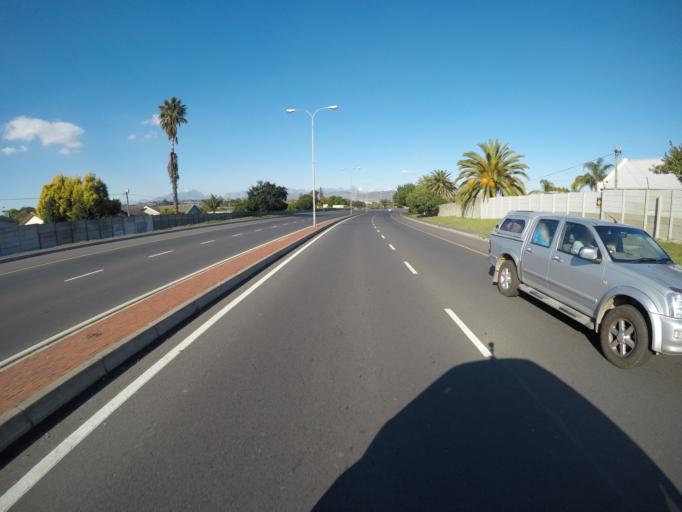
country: ZA
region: Western Cape
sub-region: City of Cape Town
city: Kraaifontein
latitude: -33.8842
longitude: 18.6684
